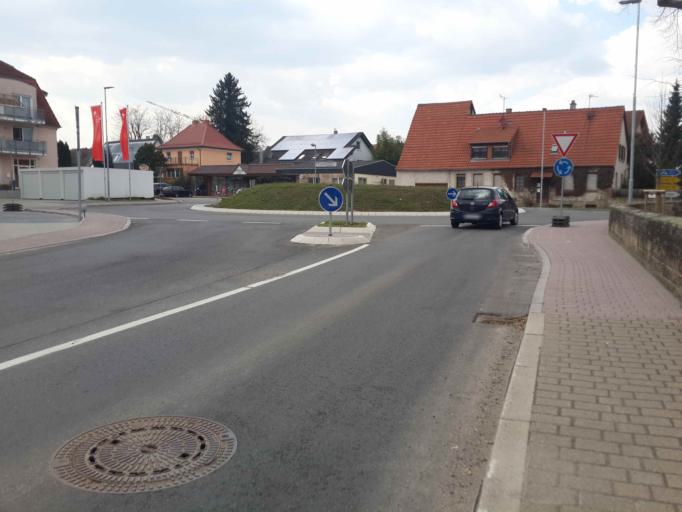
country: DE
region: Baden-Wuerttemberg
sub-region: Karlsruhe Region
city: Balzfeld
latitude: 49.2336
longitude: 8.7739
